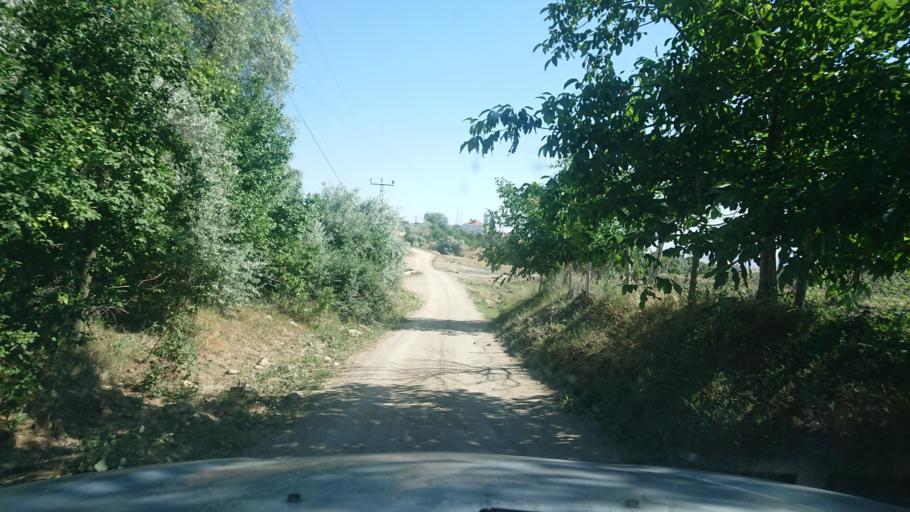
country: TR
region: Aksaray
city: Agacoren
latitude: 38.8622
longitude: 33.9124
